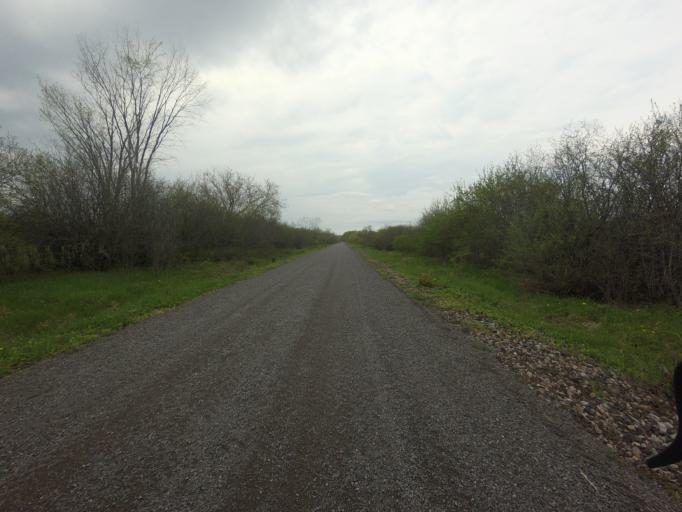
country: CA
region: Ontario
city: Carleton Place
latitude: 45.2167
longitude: -76.1832
